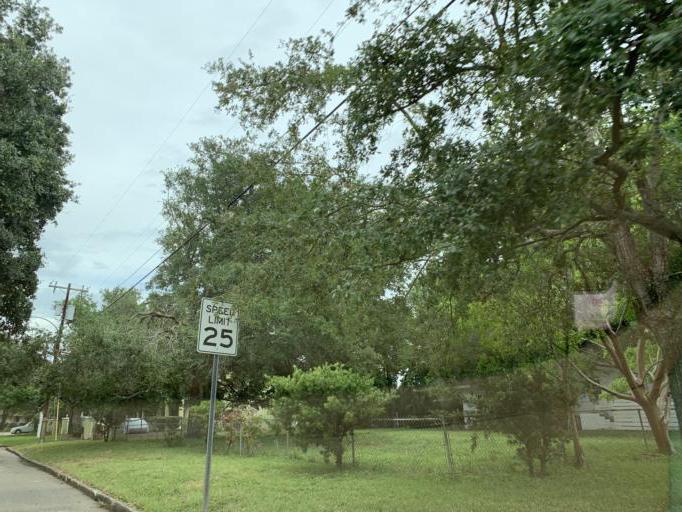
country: US
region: Florida
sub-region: Pinellas County
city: Saint Petersburg
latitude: 27.7927
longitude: -82.6155
